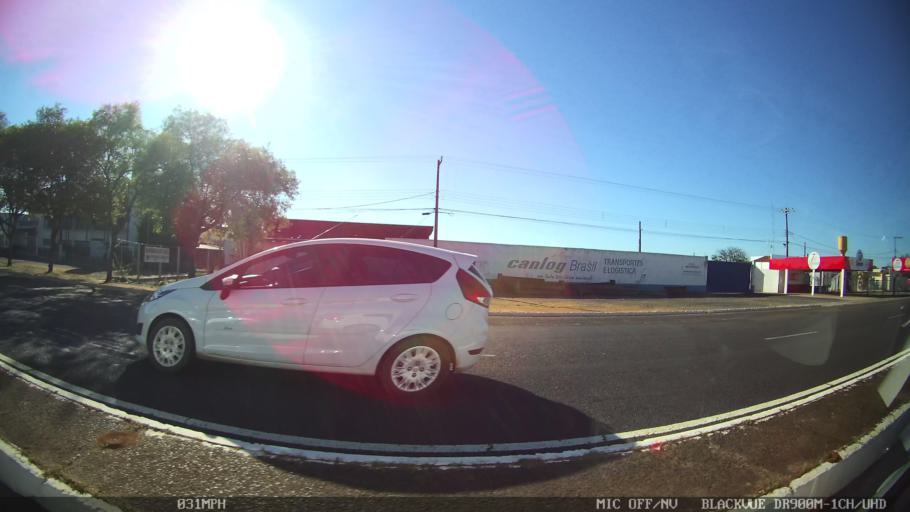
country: BR
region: Sao Paulo
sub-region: Franca
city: Franca
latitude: -20.5632
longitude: -47.3946
